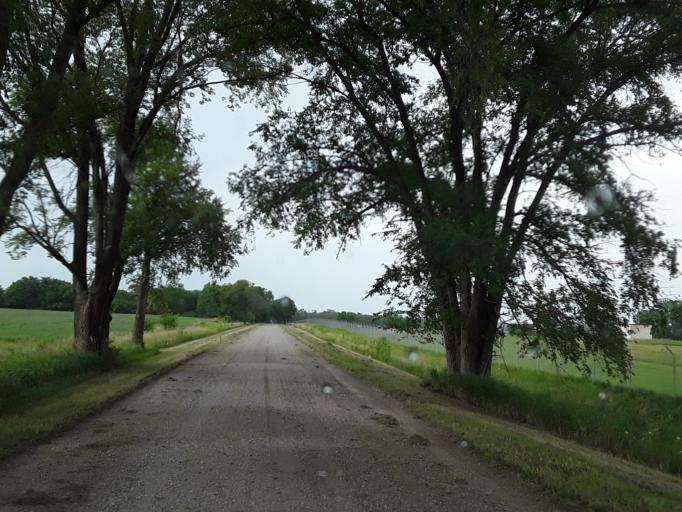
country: US
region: Nebraska
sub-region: Saunders County
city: Yutan
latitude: 41.1920
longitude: -96.4449
